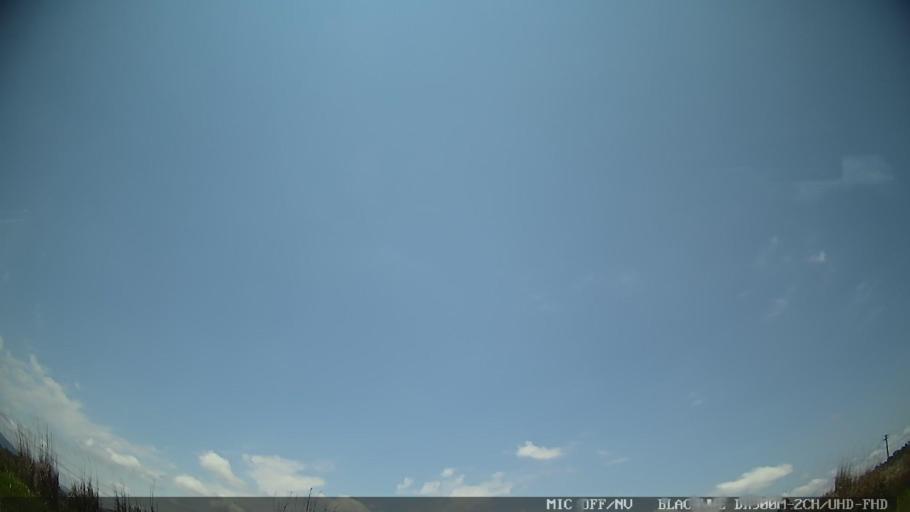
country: BR
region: Sao Paulo
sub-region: Francisco Morato
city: Francisco Morato
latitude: -23.2952
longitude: -46.7670
